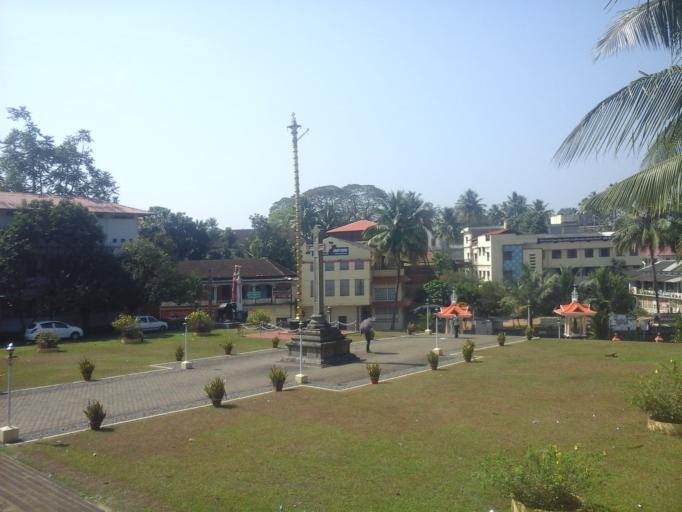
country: IN
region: Kerala
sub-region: Kottayam
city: Lalam
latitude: 9.7016
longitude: 76.7265
